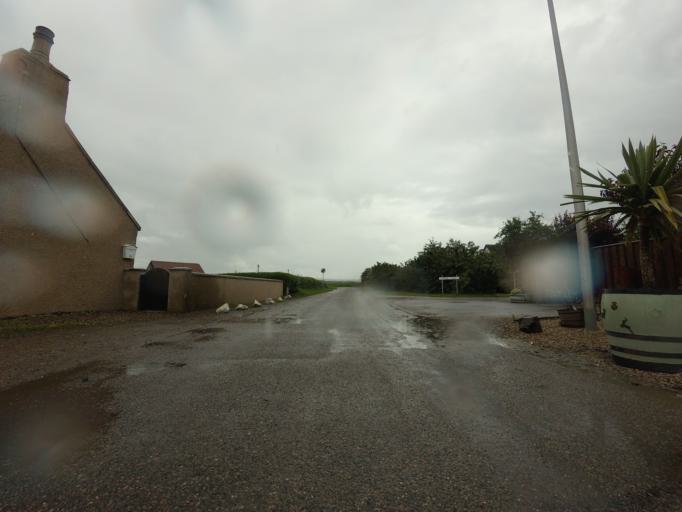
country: GB
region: Scotland
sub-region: Moray
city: Fochabers
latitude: 57.6599
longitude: -3.0733
